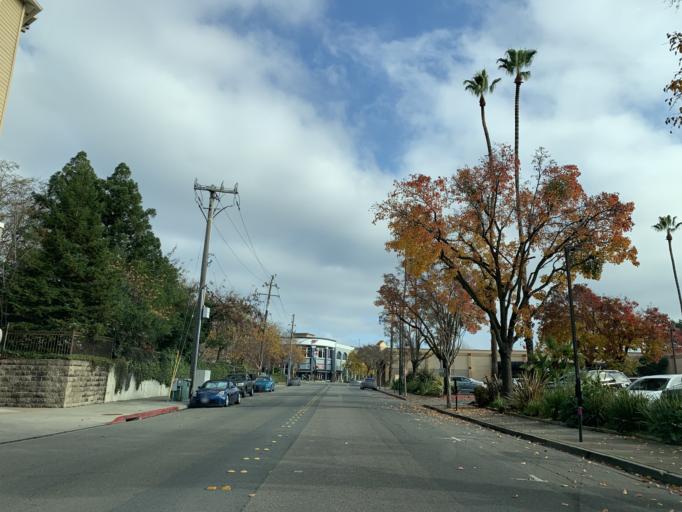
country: US
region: California
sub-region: Contra Costa County
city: Walnut Creek
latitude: 37.8939
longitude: -122.0631
